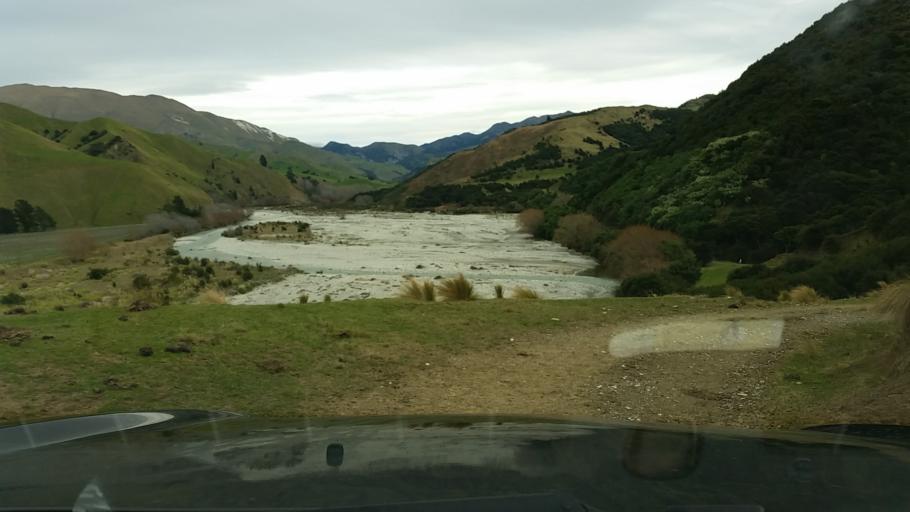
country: NZ
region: Marlborough
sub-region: Marlborough District
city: Blenheim
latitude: -41.8846
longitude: 174.0832
